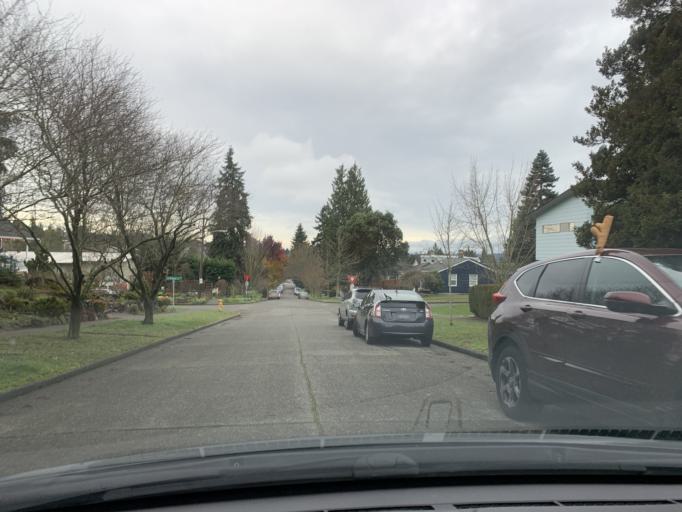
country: US
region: Washington
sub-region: King County
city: White Center
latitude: 47.5635
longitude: -122.3935
